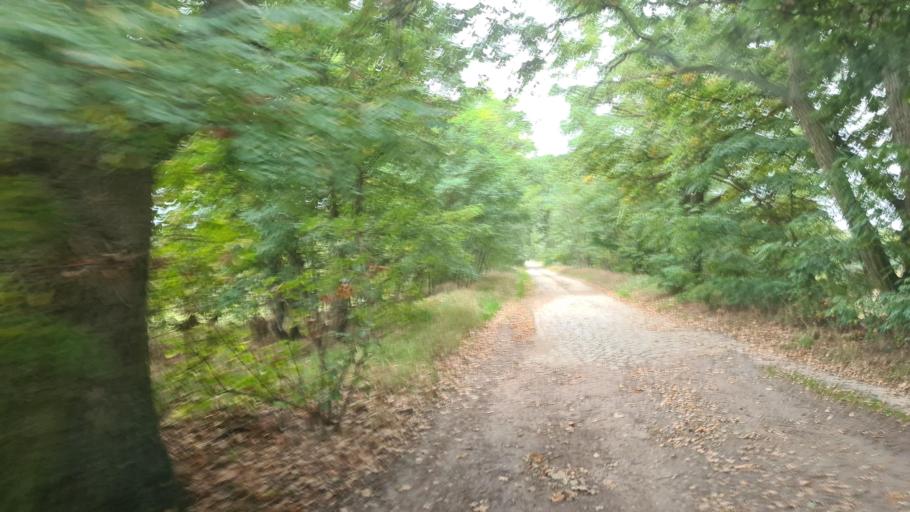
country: DE
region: Brandenburg
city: Golssen
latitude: 51.9557
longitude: 13.5815
